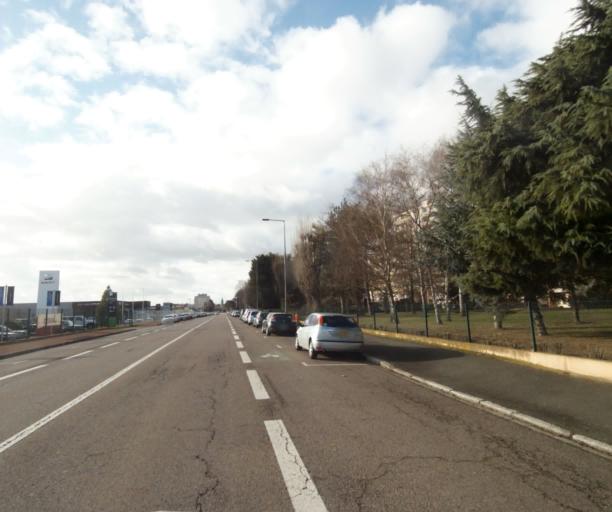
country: FR
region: Rhone-Alpes
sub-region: Departement de la Loire
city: Le Coteau
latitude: 46.0454
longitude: 4.0843
